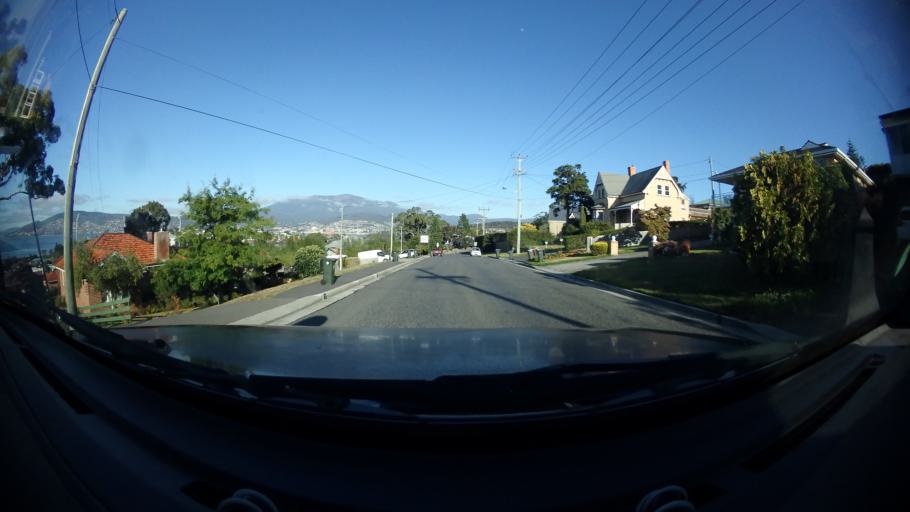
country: AU
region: Tasmania
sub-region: Clarence
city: Bellerive
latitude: -42.8734
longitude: 147.3783
